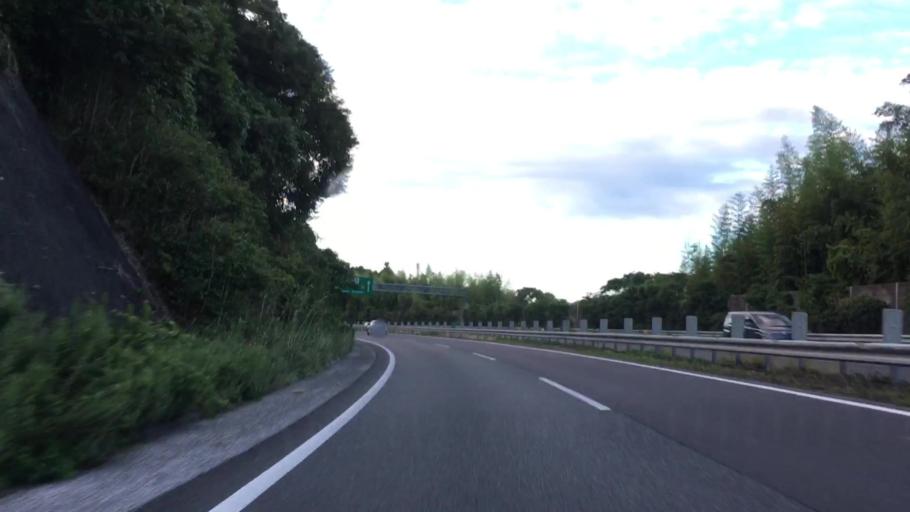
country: JP
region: Yamaguchi
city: Ogori-shimogo
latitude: 34.1682
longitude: 131.3262
